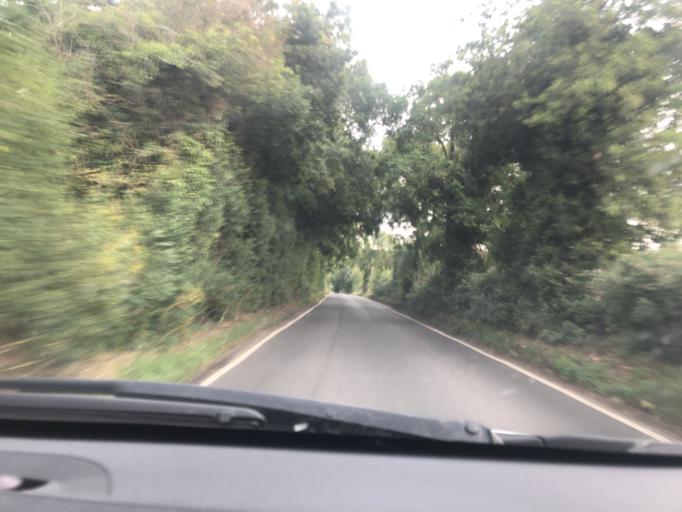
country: GB
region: England
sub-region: Kent
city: Sturry
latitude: 51.3113
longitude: 1.1369
